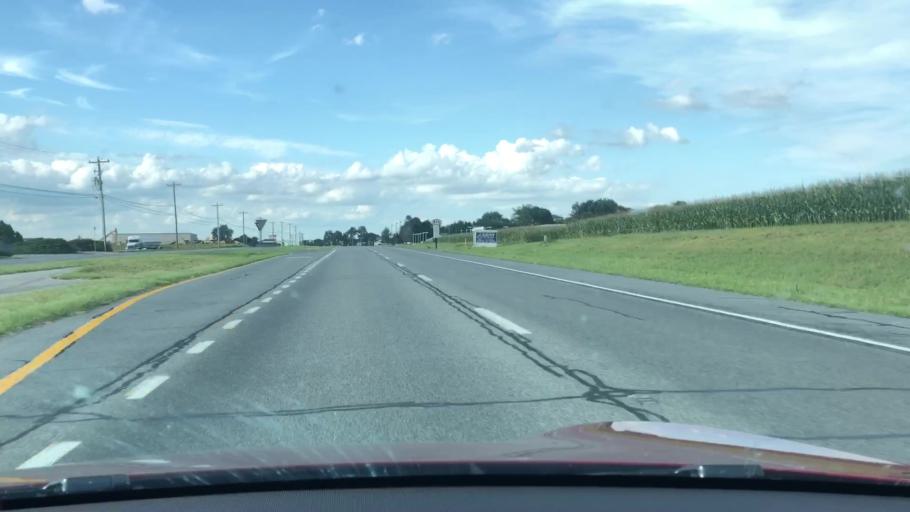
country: US
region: Delaware
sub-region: Kent County
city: Felton
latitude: 38.9783
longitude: -75.5670
